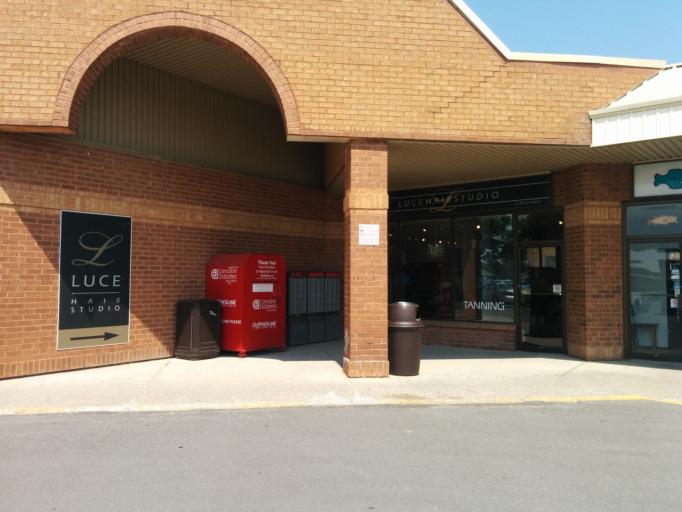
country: CA
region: Ontario
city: Kingston
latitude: 44.2586
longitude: -76.4558
